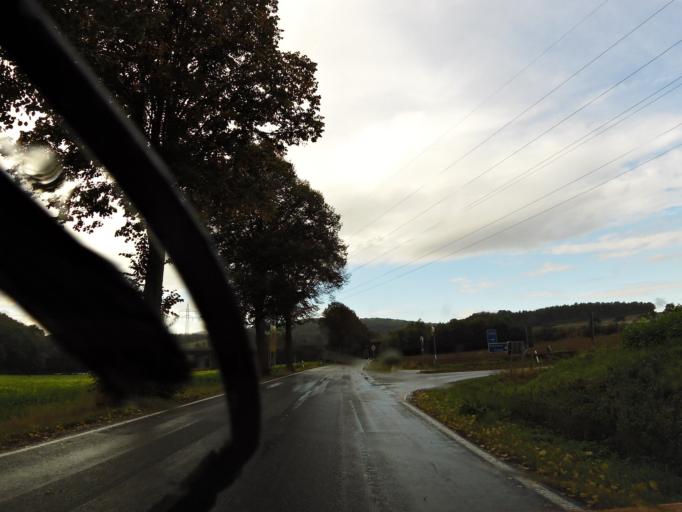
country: DE
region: Lower Saxony
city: Rosdorf
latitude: 51.4509
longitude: 9.8734
